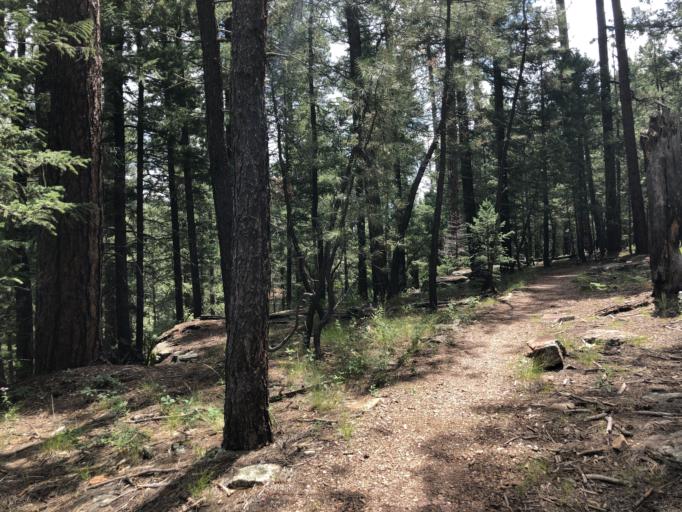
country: US
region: Arizona
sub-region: Gila County
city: Star Valley
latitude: 34.3378
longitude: -110.9514
